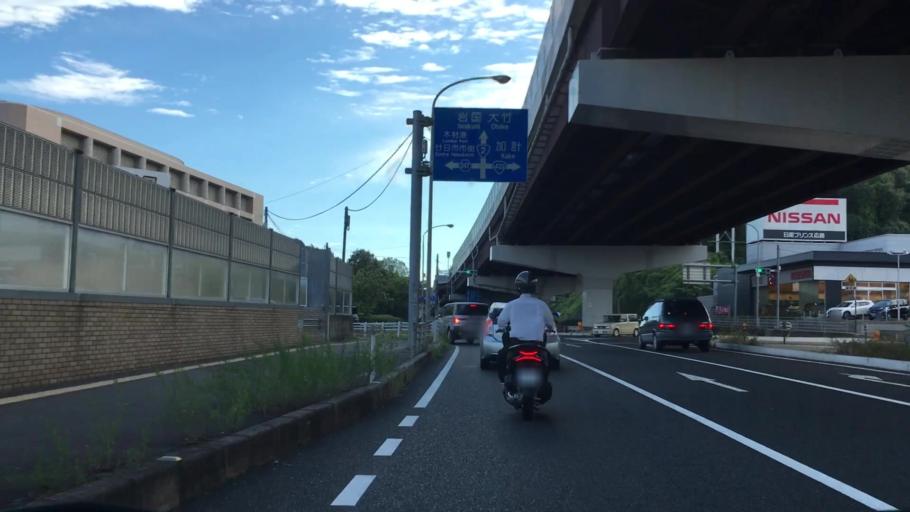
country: JP
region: Hiroshima
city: Hatsukaichi
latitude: 34.3548
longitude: 132.3227
